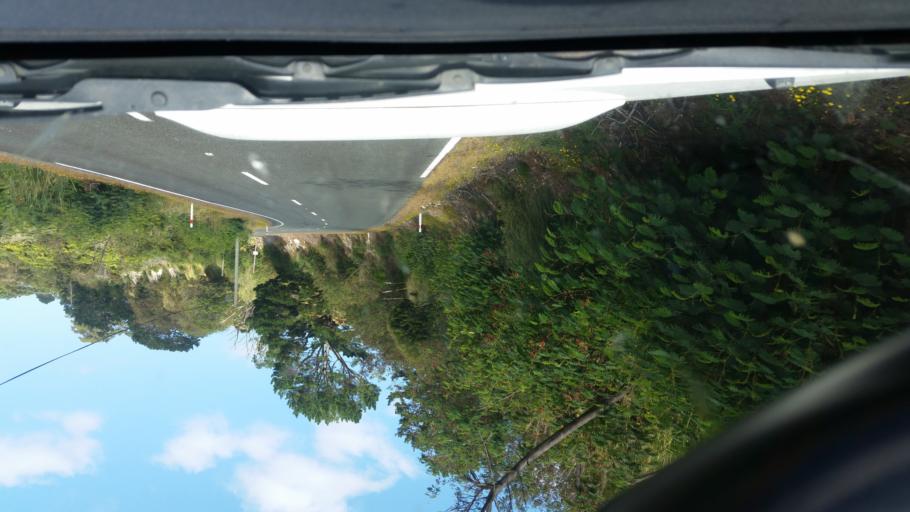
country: NZ
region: Northland
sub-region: Kaipara District
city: Dargaville
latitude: -35.8227
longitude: 173.6963
